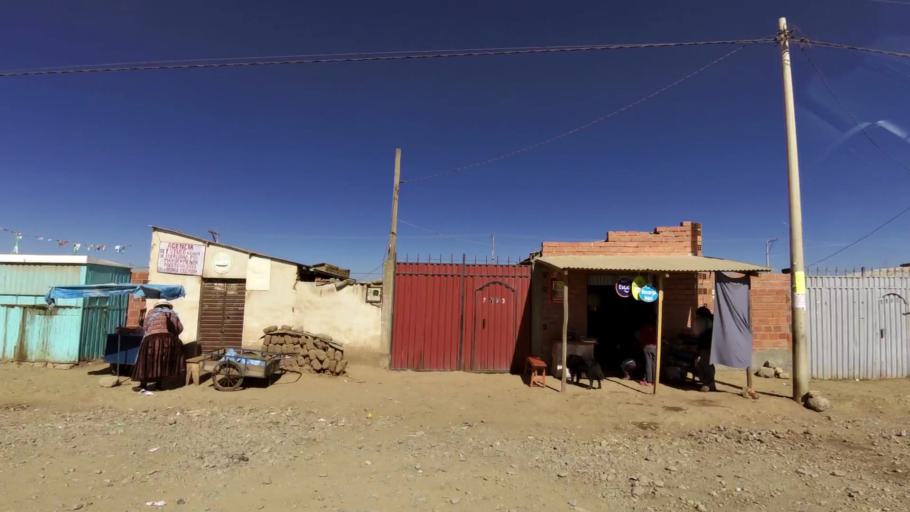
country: BO
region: La Paz
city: La Paz
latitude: -16.6065
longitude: -68.1991
